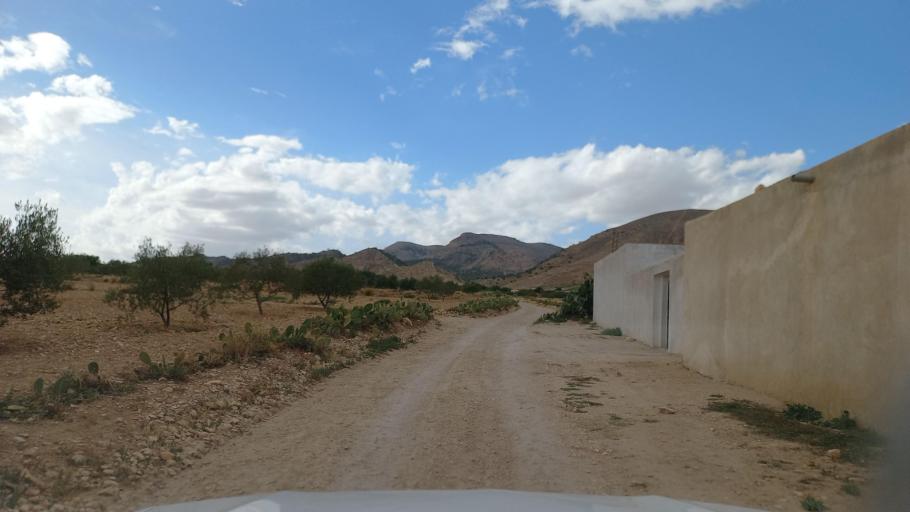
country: TN
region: Al Qasrayn
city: Sbiba
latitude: 35.4494
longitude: 9.0707
